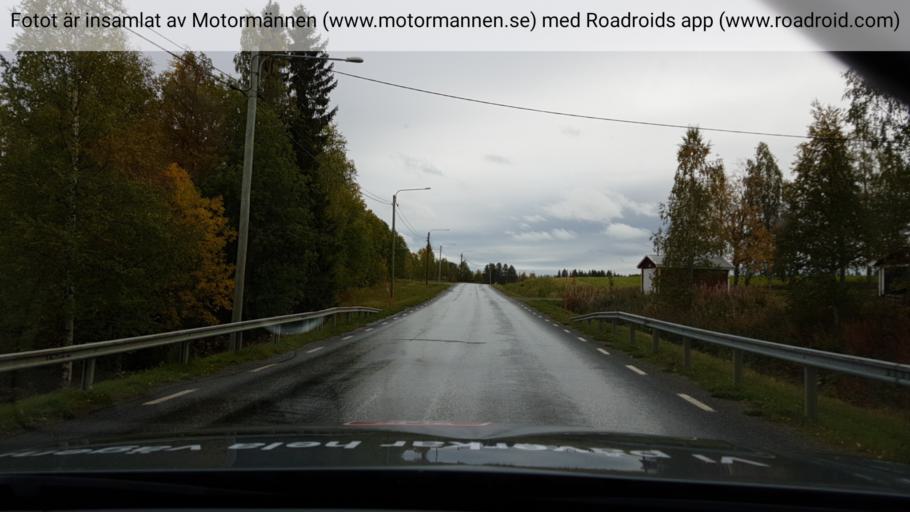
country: SE
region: Vaesterbotten
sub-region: Vilhelmina Kommun
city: Sjoberg
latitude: 64.6440
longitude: 16.3529
